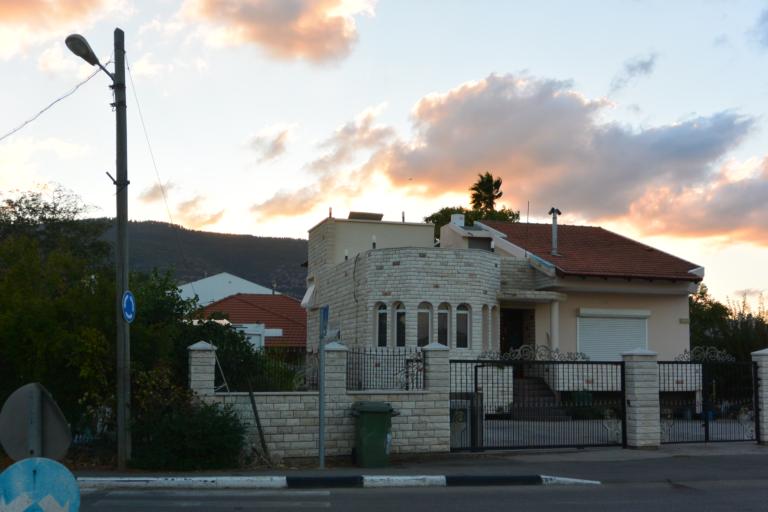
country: IL
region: Haifa
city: Rekhasim
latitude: 32.7503
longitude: 35.0879
